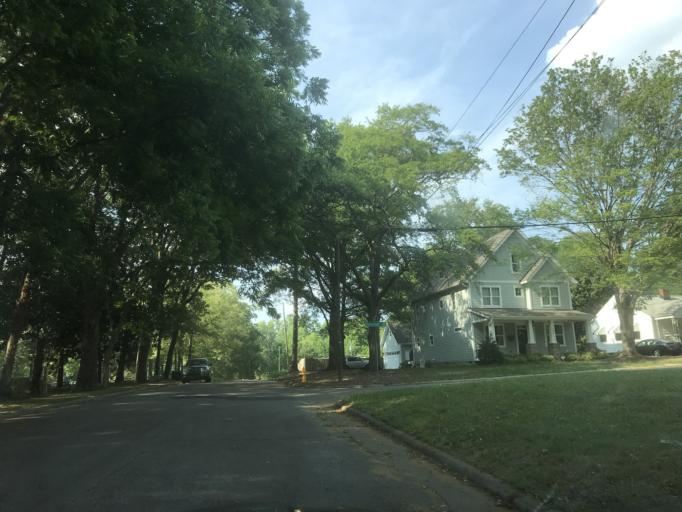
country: US
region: North Carolina
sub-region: Wake County
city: Raleigh
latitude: 35.7899
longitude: -78.6228
